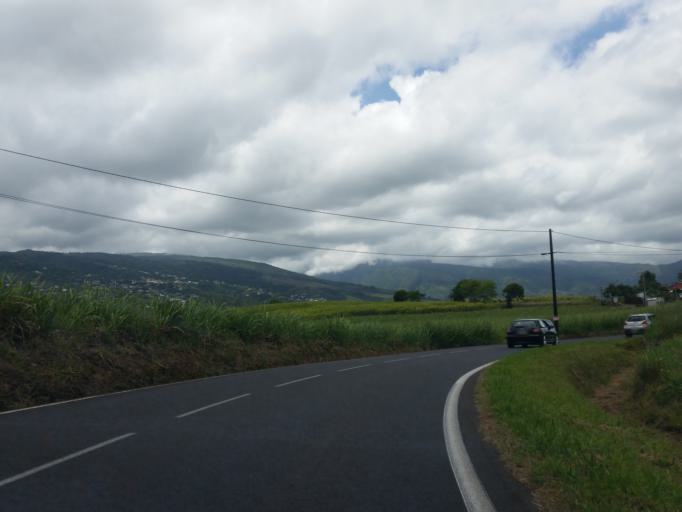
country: RE
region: Reunion
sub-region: Reunion
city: Sainte-Marie
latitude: -20.9222
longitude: 55.5397
